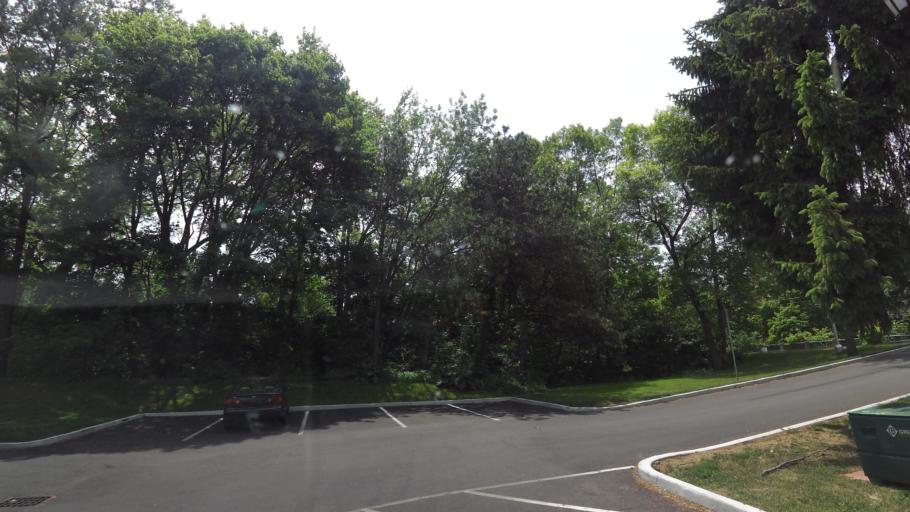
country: CA
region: Ontario
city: Oakville
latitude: 43.4619
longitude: -79.6504
